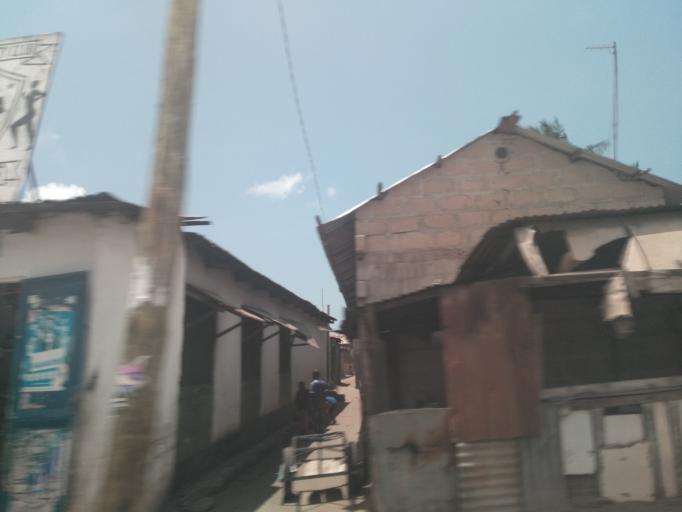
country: TZ
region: Dar es Salaam
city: Dar es Salaam
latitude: -6.8703
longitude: 39.2805
